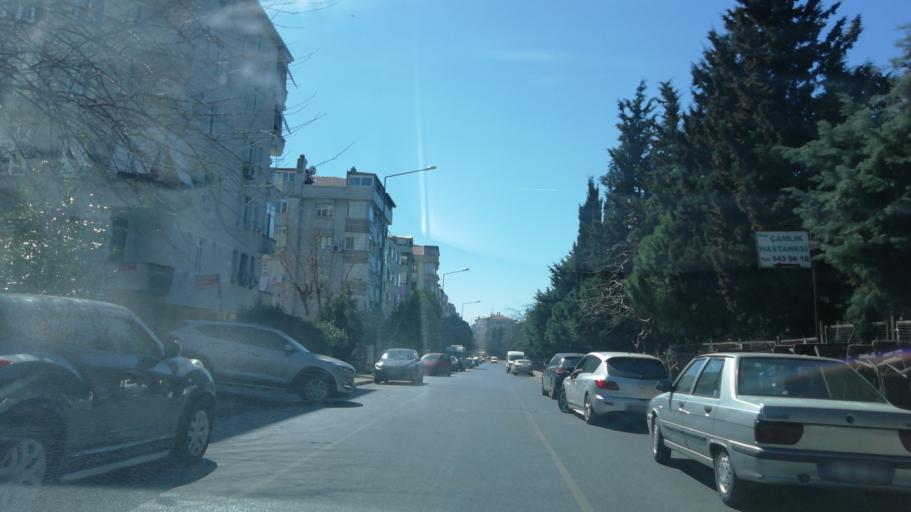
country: TR
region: Istanbul
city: Bahcelievler
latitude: 40.9904
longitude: 28.8668
